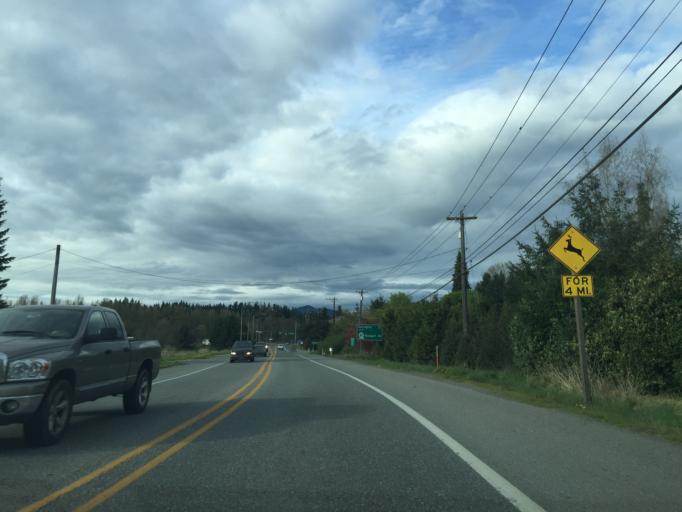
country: US
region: Washington
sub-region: Snohomish County
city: Arlington
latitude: 48.2055
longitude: -122.1172
